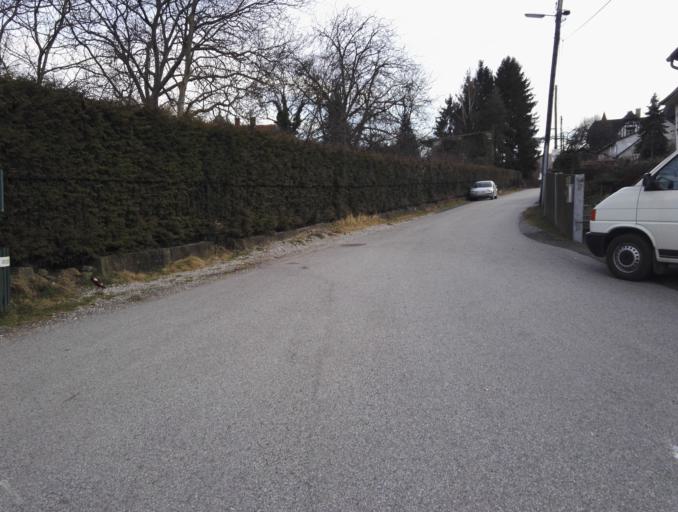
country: AT
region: Styria
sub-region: Graz Stadt
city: Goesting
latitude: 47.1059
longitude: 15.3936
